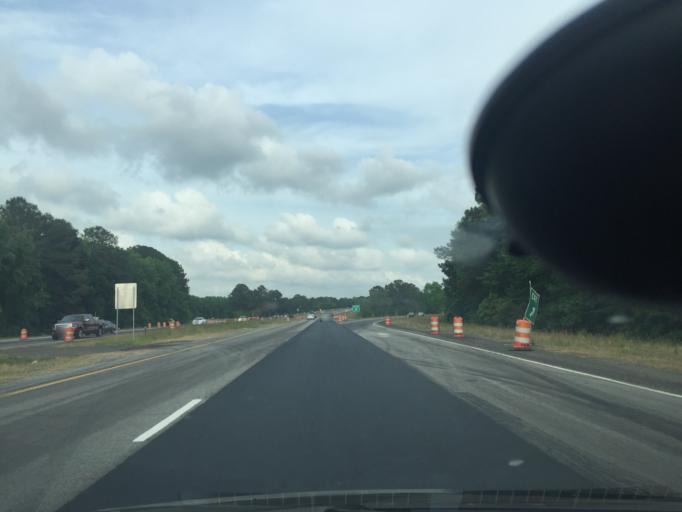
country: US
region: Georgia
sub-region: Chatham County
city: Georgetown
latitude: 32.0012
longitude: -81.2552
